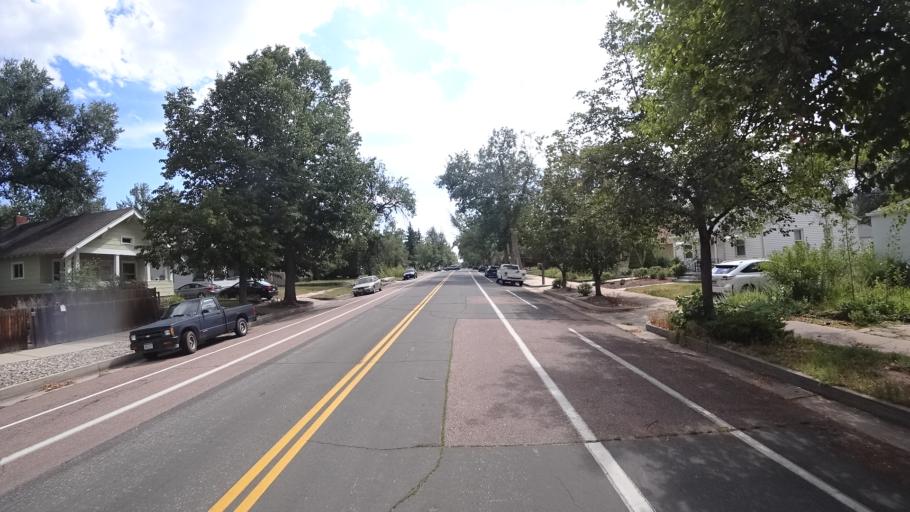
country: US
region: Colorado
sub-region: El Paso County
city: Colorado Springs
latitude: 38.8511
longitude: -104.8074
